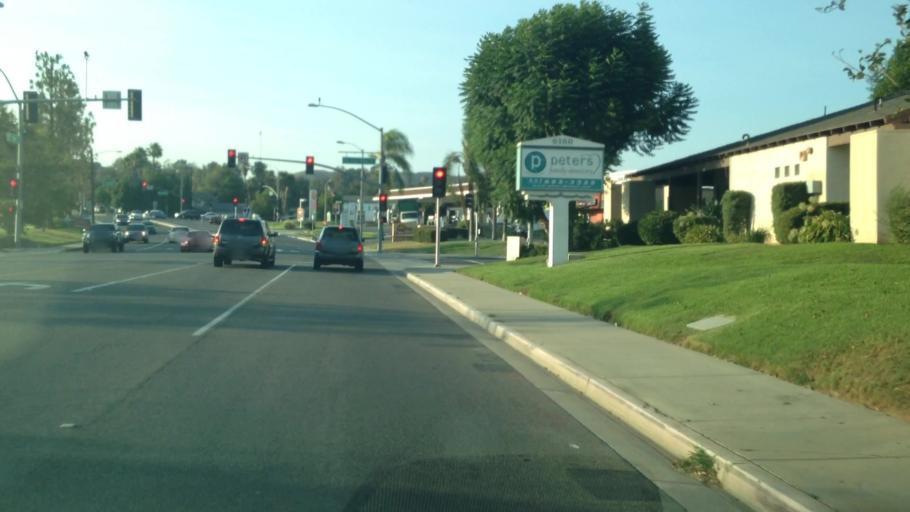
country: US
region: California
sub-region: Riverside County
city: Pedley
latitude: 33.9756
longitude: -117.4622
